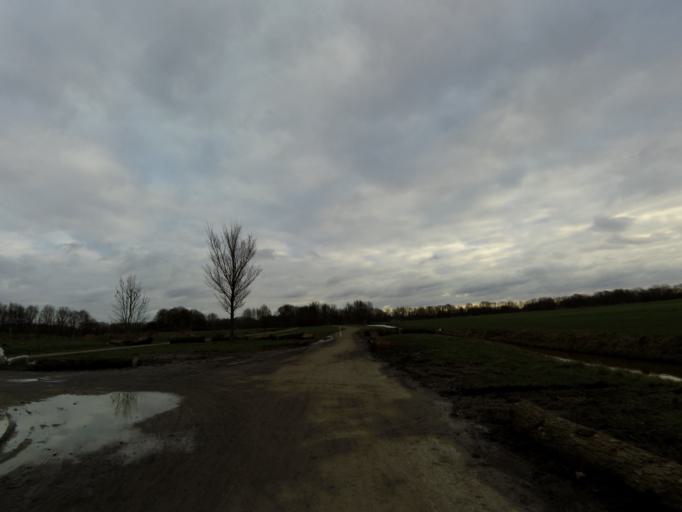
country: NL
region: South Holland
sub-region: Gemeente Leiden
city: Leiden
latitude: 52.1410
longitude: 4.4962
